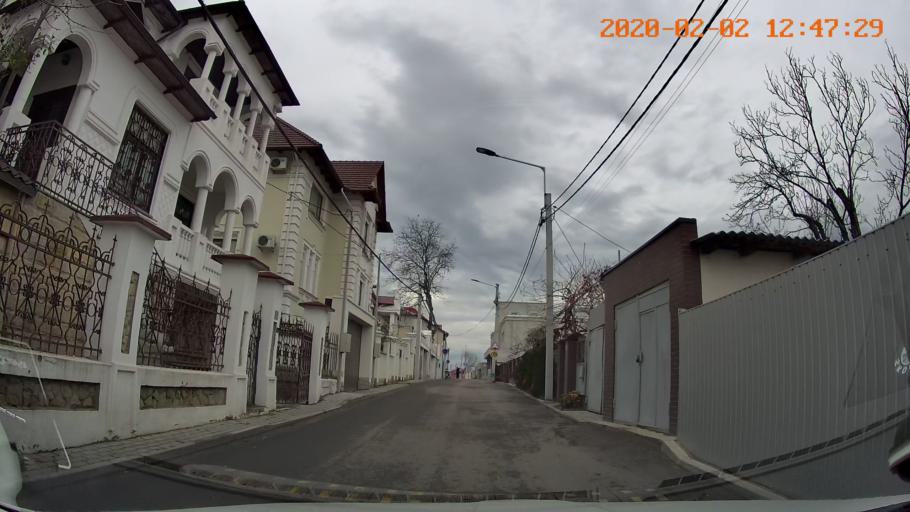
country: MD
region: Chisinau
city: Chisinau
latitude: 47.0128
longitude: 28.8238
